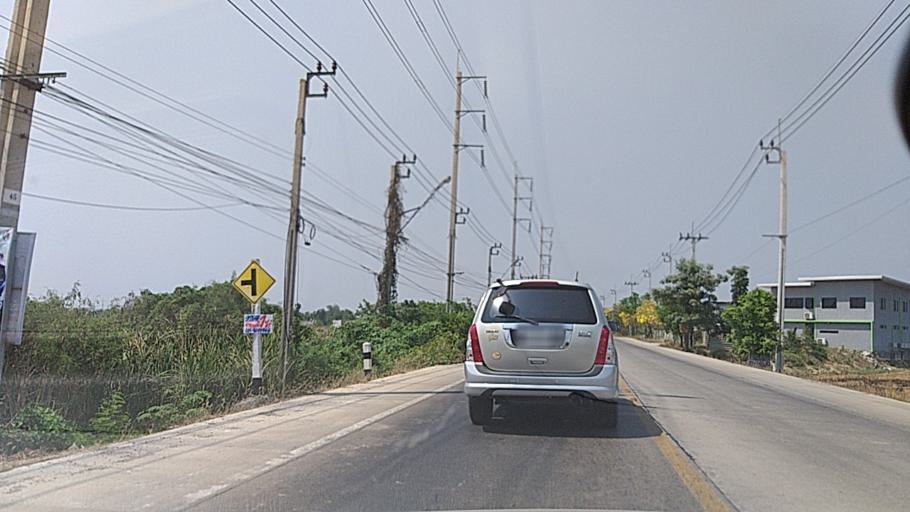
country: TH
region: Nonthaburi
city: Sai Noi
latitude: 13.9651
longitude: 100.3106
